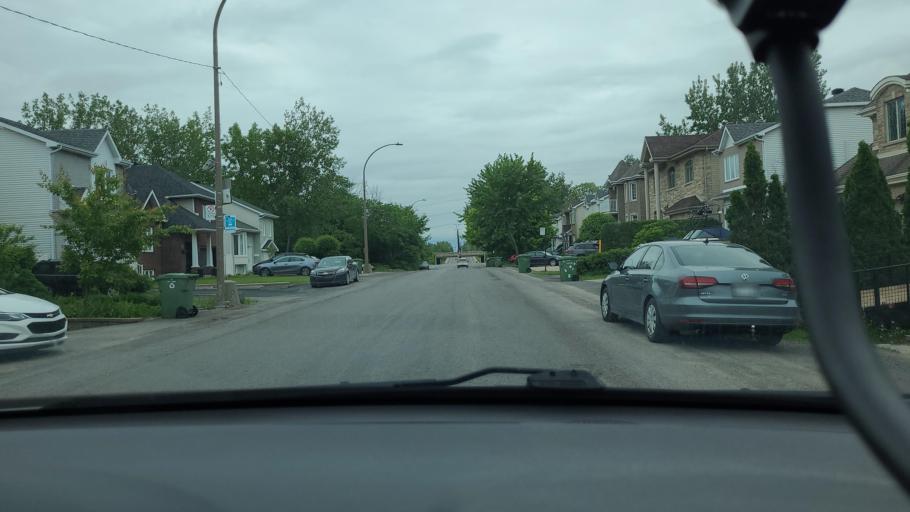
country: CA
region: Quebec
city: Montreal-Est
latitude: 45.6667
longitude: -73.5366
